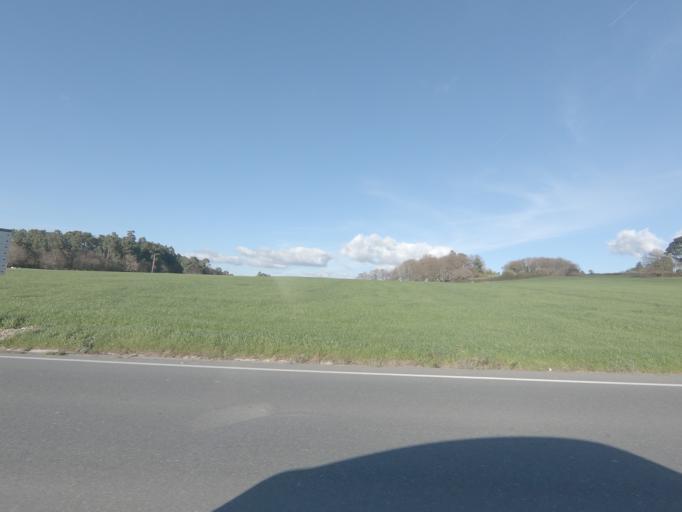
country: ES
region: Galicia
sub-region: Provincia de Pontevedra
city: Silleda
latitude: 42.7086
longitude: -8.2695
